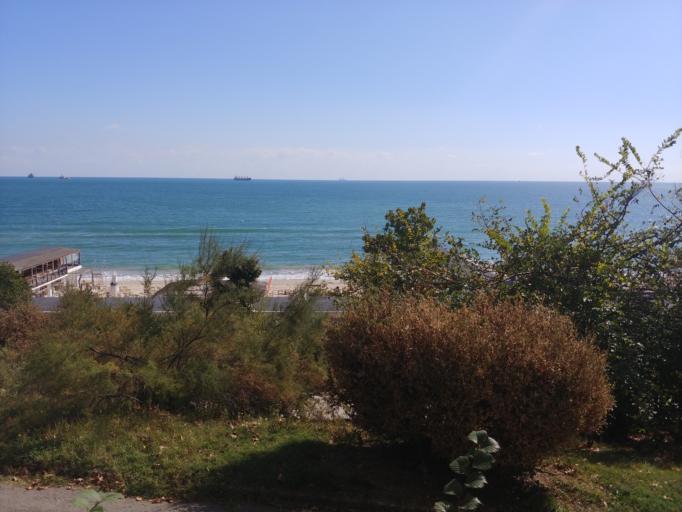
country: BG
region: Varna
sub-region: Obshtina Varna
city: Varna
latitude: 43.2033
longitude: 27.9240
